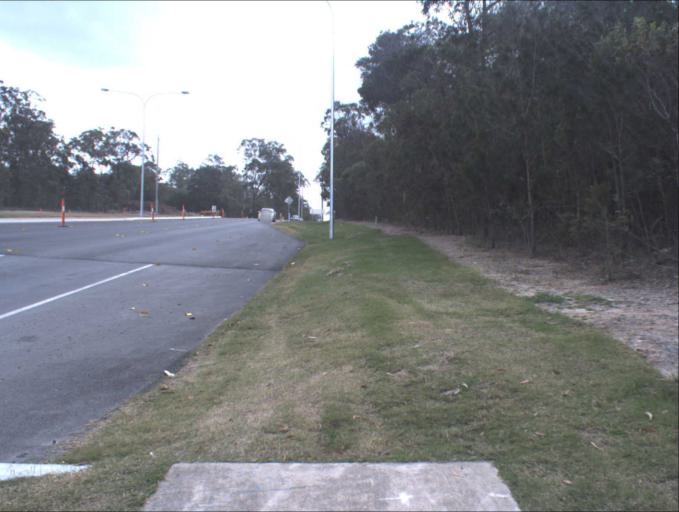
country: AU
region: Queensland
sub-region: Logan
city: Logan Reserve
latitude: -27.7085
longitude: 153.0929
